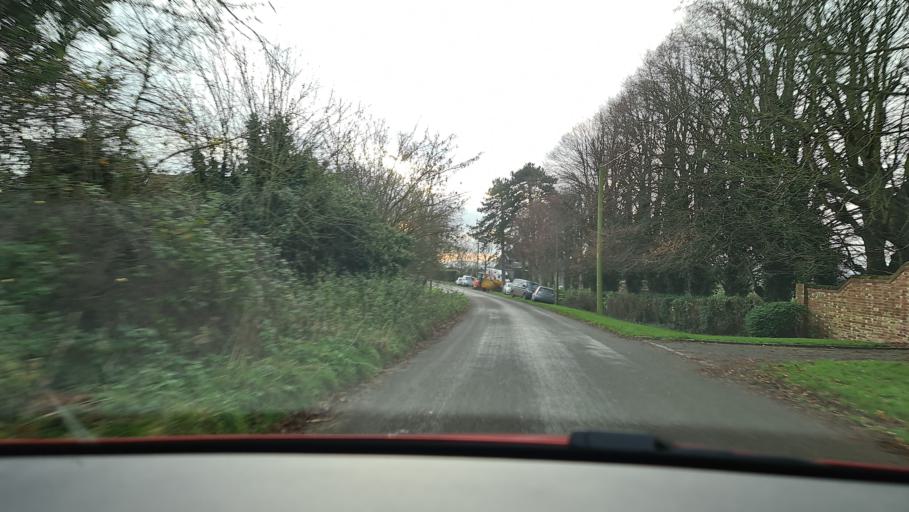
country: GB
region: England
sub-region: Buckinghamshire
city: Long Crendon
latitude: 51.7920
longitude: -0.9656
